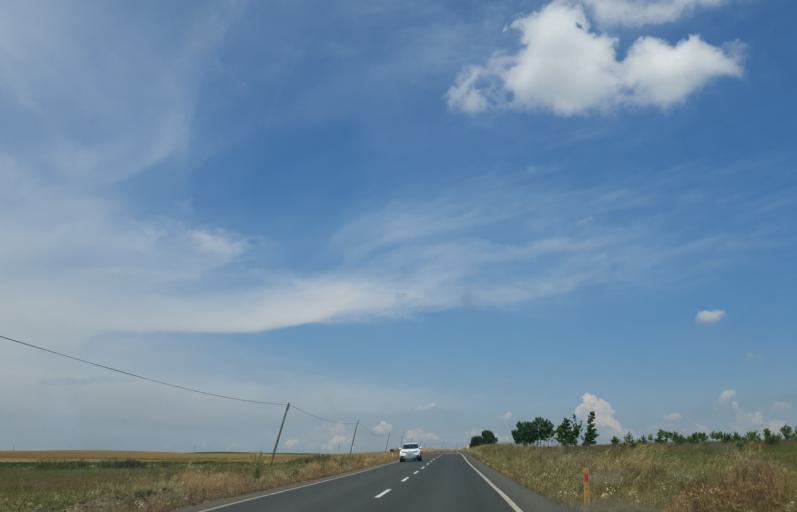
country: TR
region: Kirklareli
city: Buyukkaristiran
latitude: 41.2438
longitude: 27.6024
